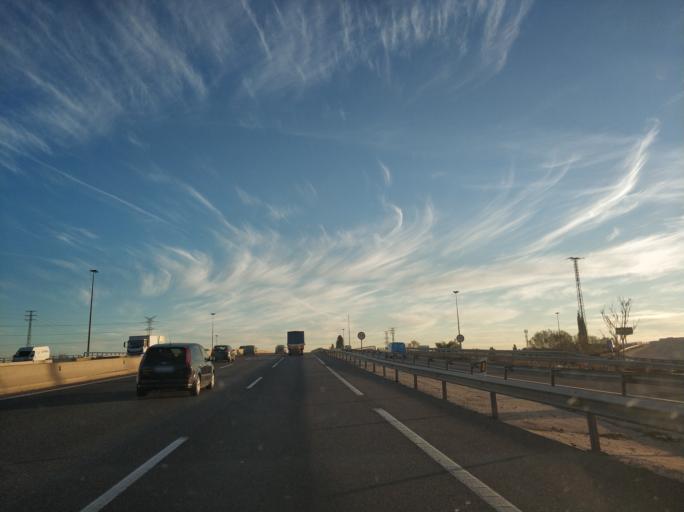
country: ES
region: Madrid
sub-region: Provincia de Madrid
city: Pinto
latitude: 40.2781
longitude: -3.6910
